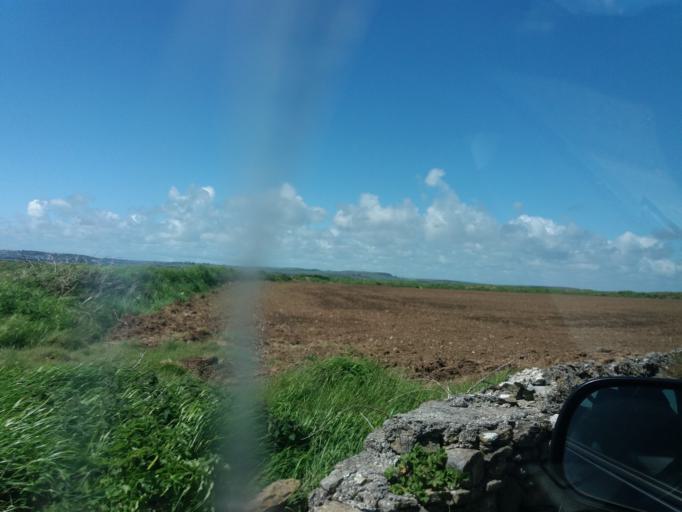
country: IE
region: Munster
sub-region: Waterford
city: Dunmore East
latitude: 52.1307
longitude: -6.9301
